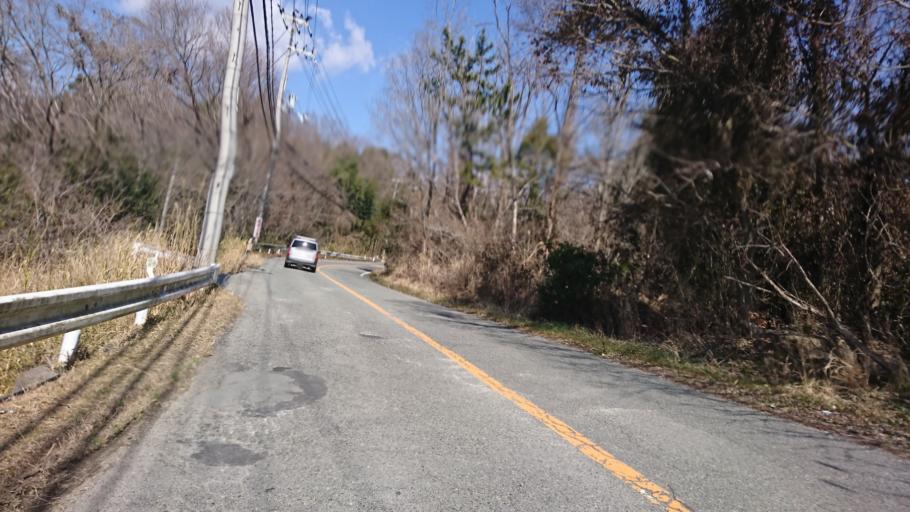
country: JP
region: Hyogo
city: Kakogawacho-honmachi
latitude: 34.8303
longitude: 134.8217
